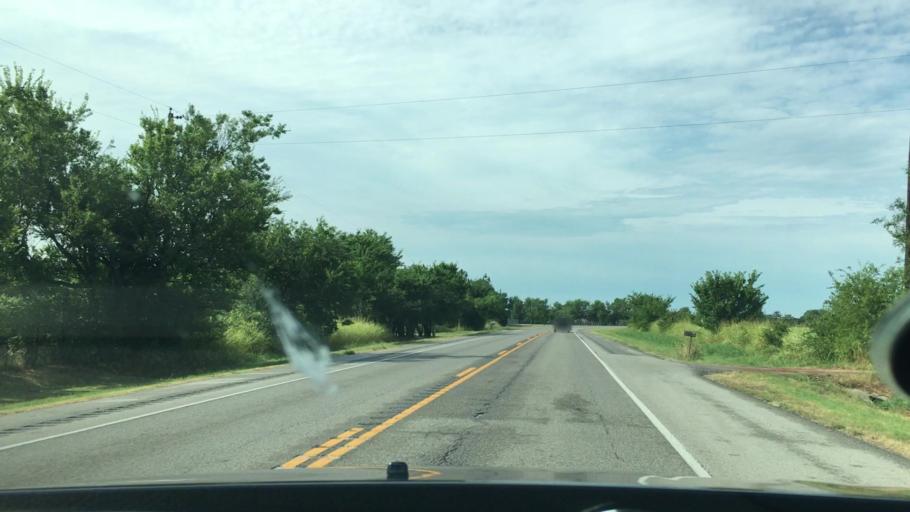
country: US
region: Oklahoma
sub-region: Murray County
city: Sulphur
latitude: 34.5338
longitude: -96.9674
